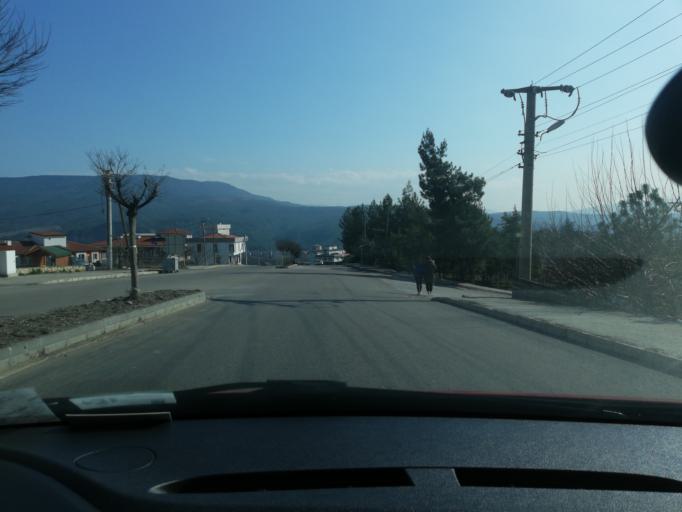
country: TR
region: Karabuk
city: Safranbolu
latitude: 41.2316
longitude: 32.6685
